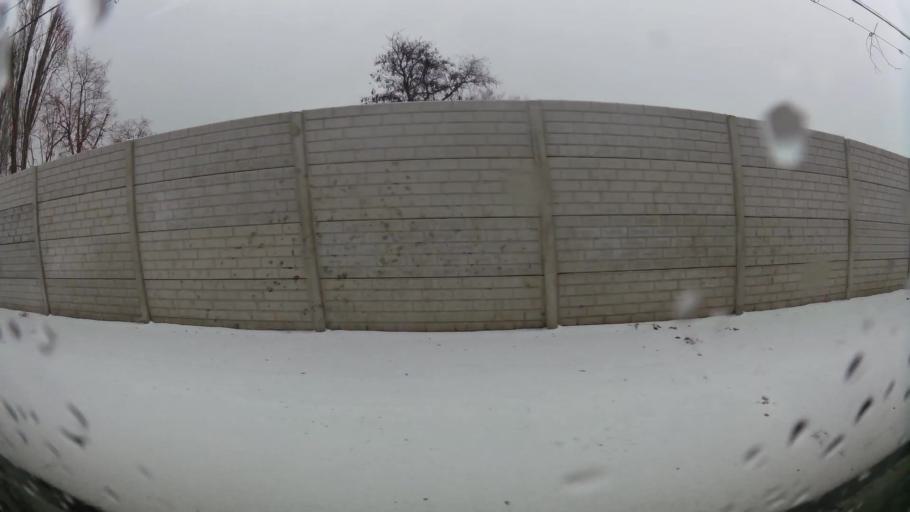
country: RO
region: Prahova
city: Ploiesti
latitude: 44.9254
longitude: 26.0064
